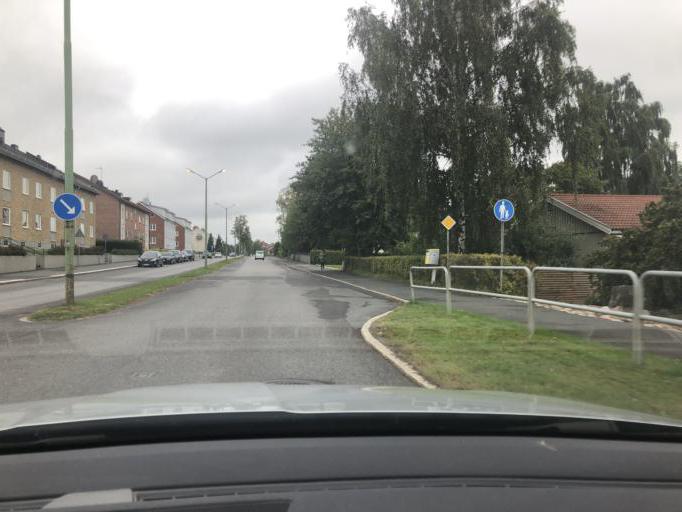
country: SE
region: Joenkoeping
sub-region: Varnamo Kommun
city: Varnamo
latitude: 57.1782
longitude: 14.0326
